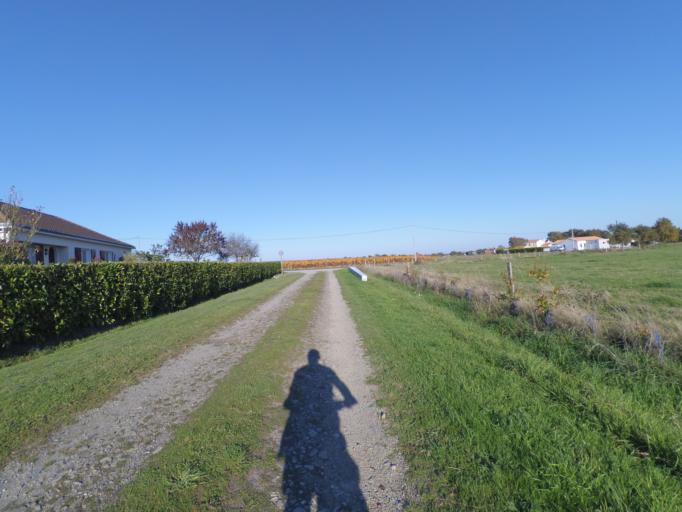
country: FR
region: Pays de la Loire
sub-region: Departement de la Loire-Atlantique
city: Remouille
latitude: 47.0313
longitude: -1.3929
